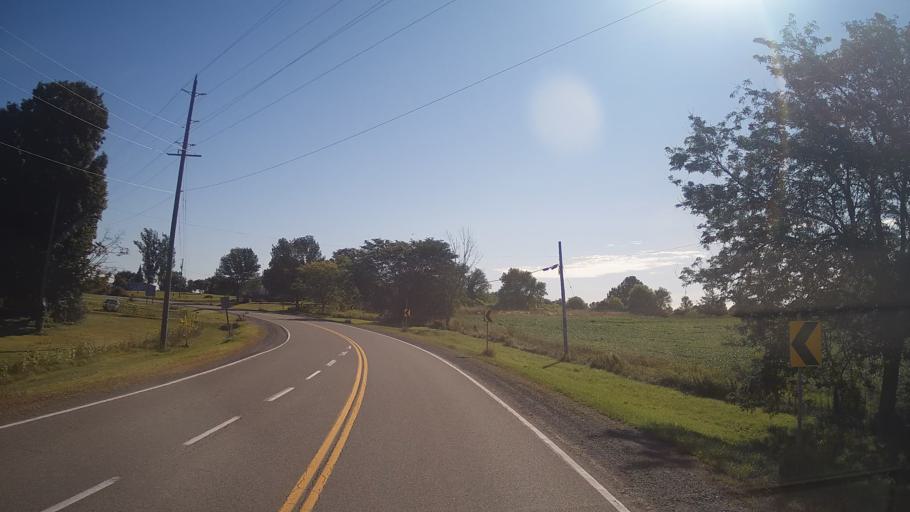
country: CA
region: Ontario
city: Gananoque
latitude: 44.5955
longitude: -76.0884
